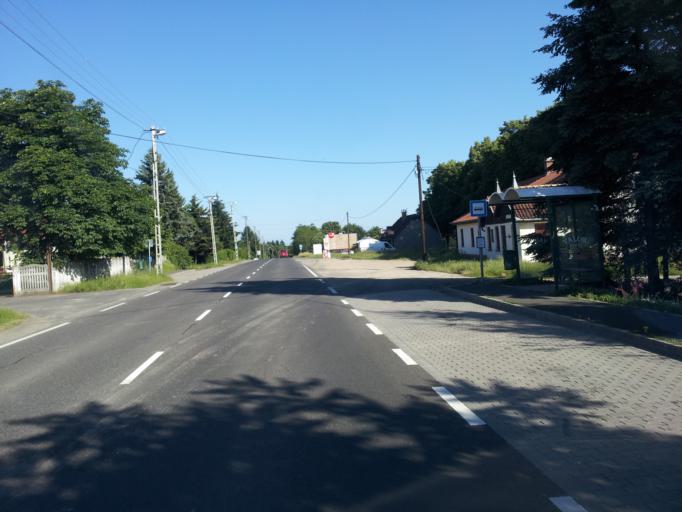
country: HU
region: Nograd
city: Nagyoroszi
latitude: 47.9940
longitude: 19.1013
